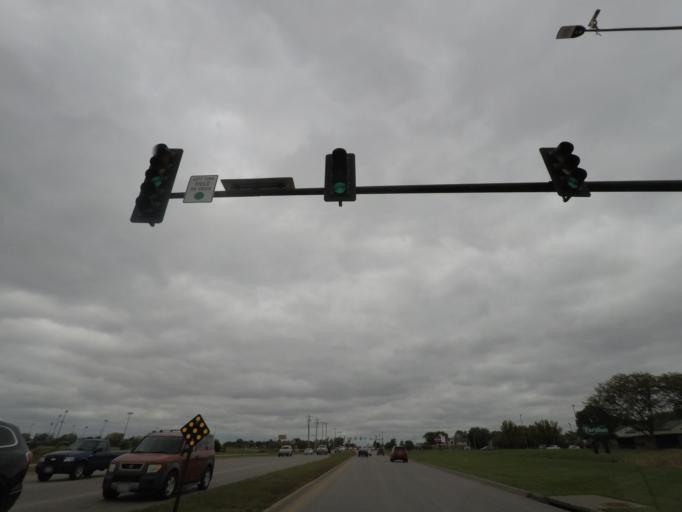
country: US
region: Iowa
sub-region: Polk County
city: Ankeny
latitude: 41.7175
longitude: -93.6004
